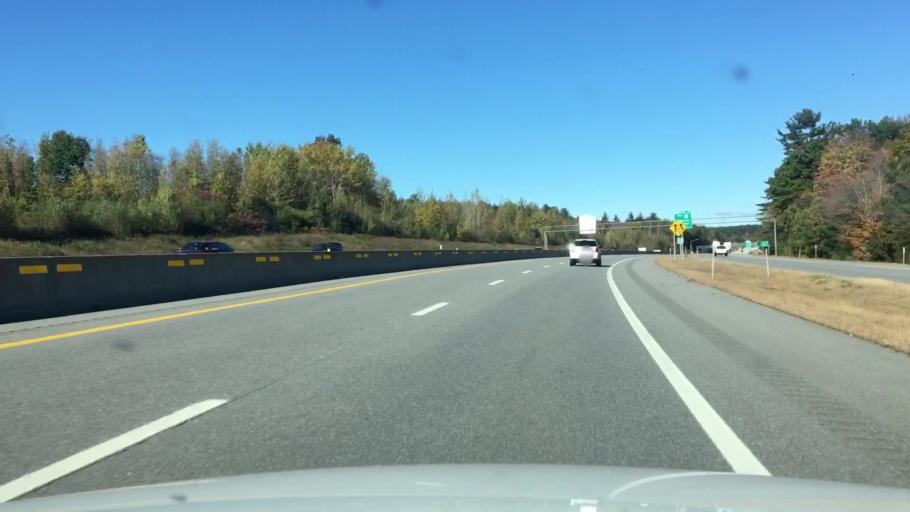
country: US
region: New Hampshire
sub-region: Strafford County
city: Rochester
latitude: 43.2840
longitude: -70.9827
